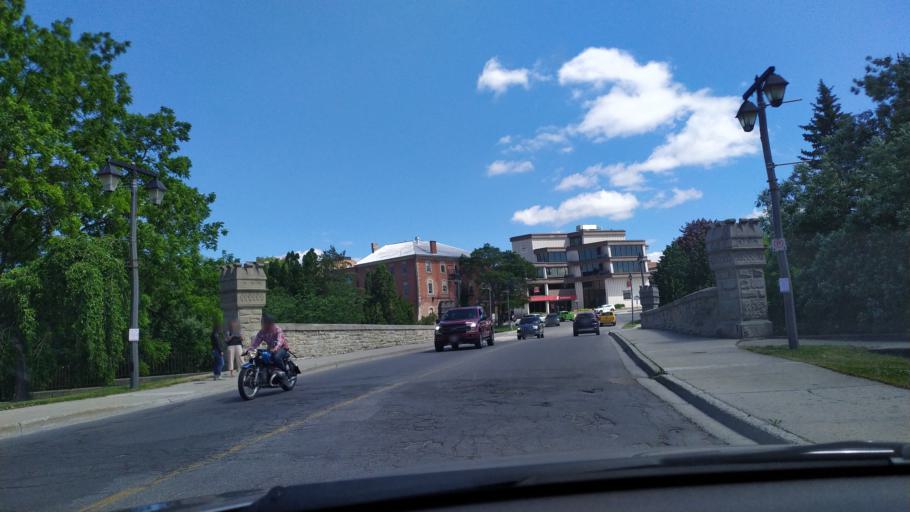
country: CA
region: Ontario
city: Stratford
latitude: 43.3726
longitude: -80.9852
